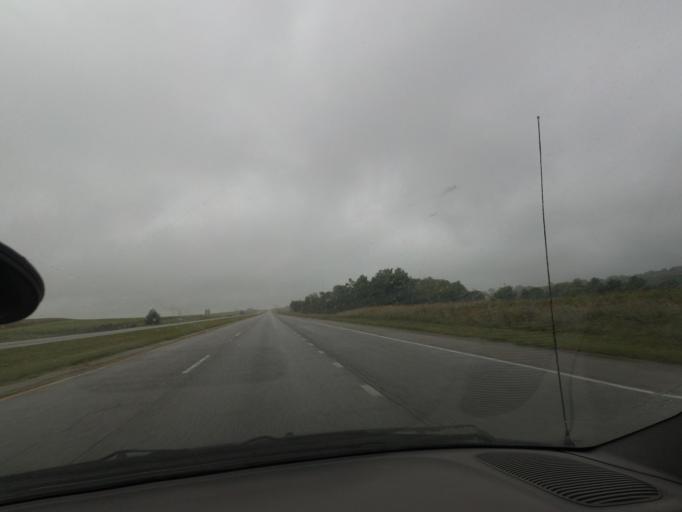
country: US
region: Illinois
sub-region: Pike County
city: Barry
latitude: 39.7031
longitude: -91.0347
